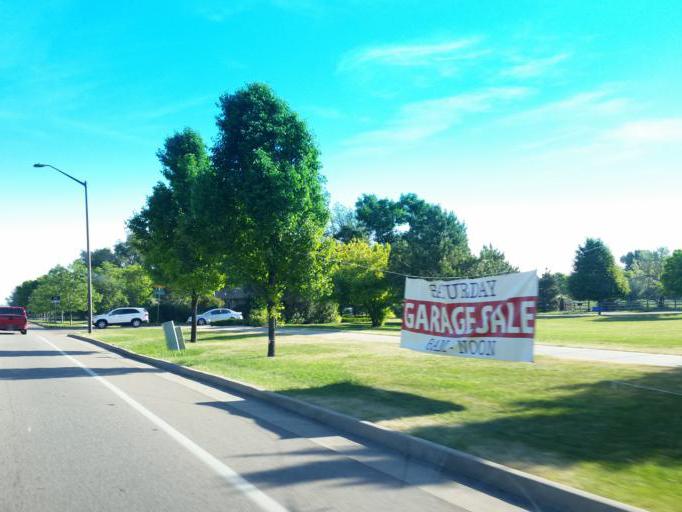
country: US
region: Colorado
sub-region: Larimer County
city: Fort Collins
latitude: 40.5337
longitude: -105.0202
